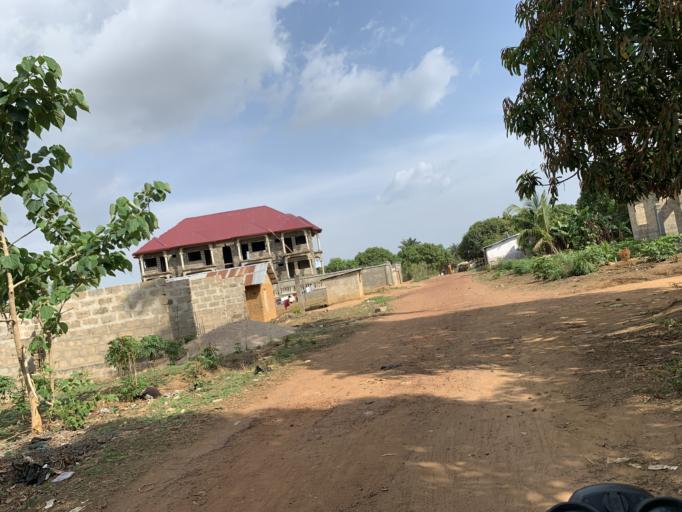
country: SL
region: Western Area
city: Waterloo
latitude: 8.3428
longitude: -13.0465
